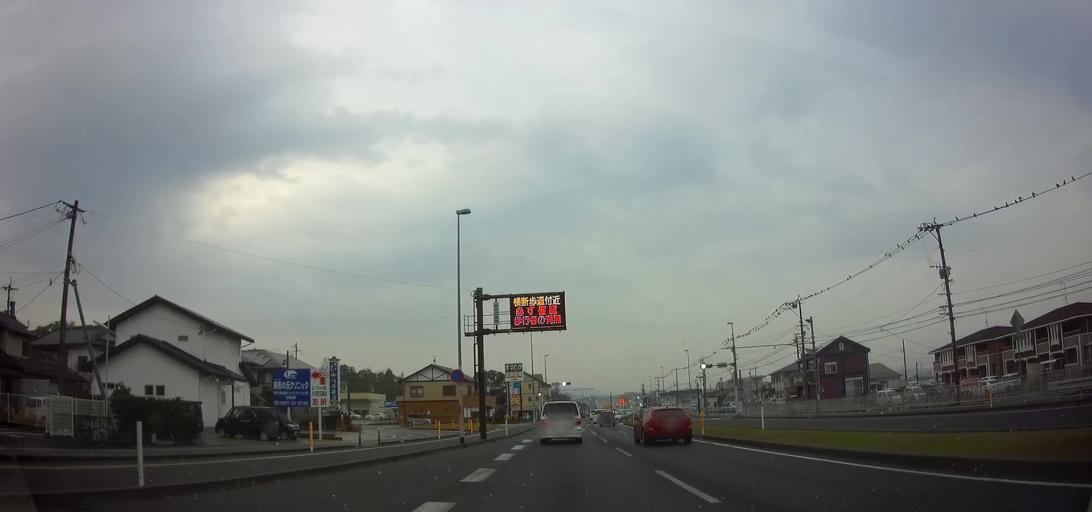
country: JP
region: Nagasaki
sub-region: Isahaya-shi
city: Isahaya
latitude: 32.8337
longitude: 130.0878
